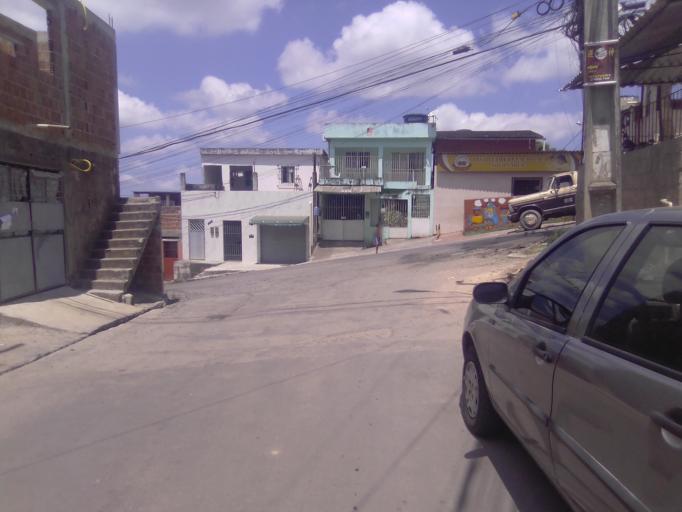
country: BR
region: Pernambuco
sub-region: Jaboatao Dos Guararapes
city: Jaboatao dos Guararapes
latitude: -8.0665
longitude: -34.9983
